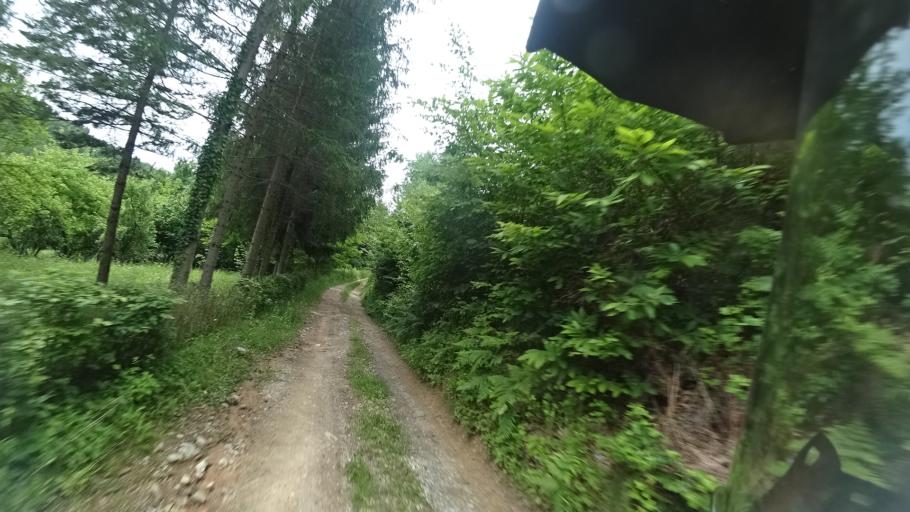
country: HR
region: Karlovacka
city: Vojnic
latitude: 45.2432
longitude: 15.6315
